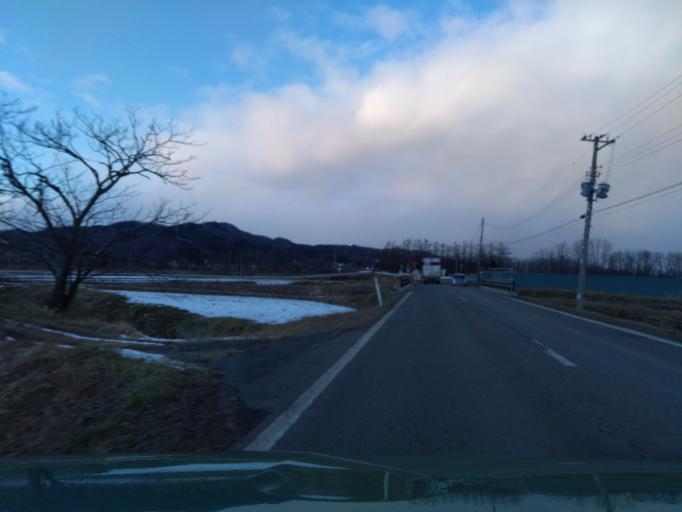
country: JP
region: Iwate
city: Shizukuishi
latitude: 39.6934
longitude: 141.0651
